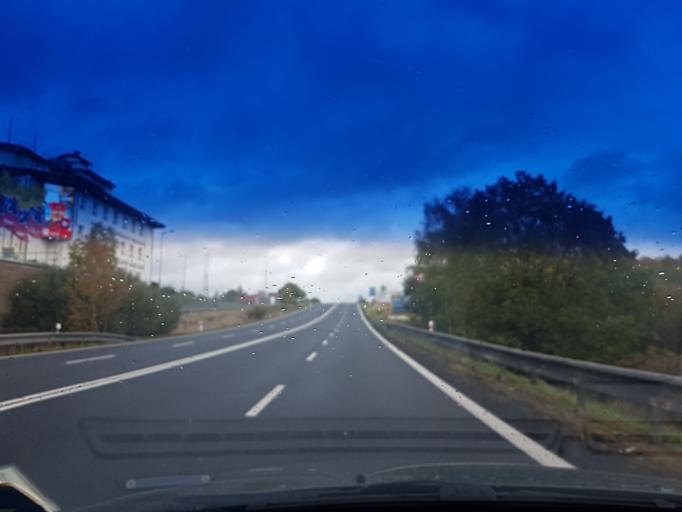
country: DE
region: Bavaria
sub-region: Upper Franconia
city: Schirnding
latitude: 50.0868
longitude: 12.2597
